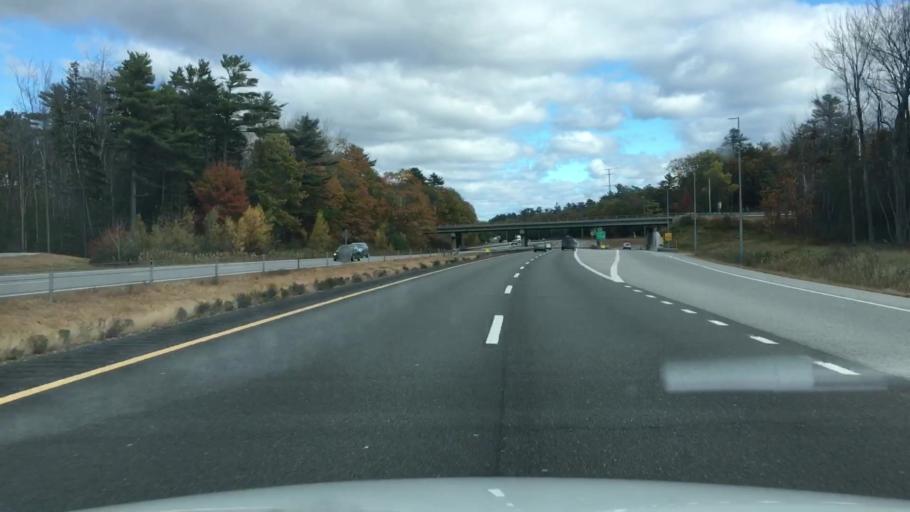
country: US
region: Maine
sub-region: Cumberland County
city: Yarmouth
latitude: 43.7836
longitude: -70.1923
